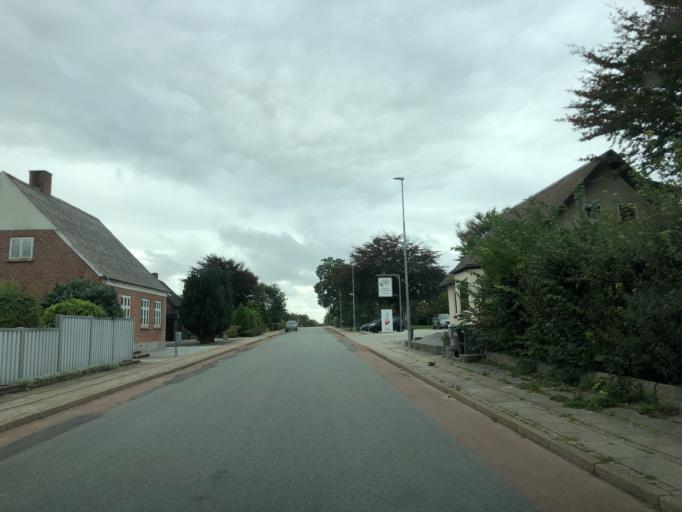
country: DK
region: North Denmark
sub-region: Thisted Kommune
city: Thisted
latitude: 56.8875
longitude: 8.5910
